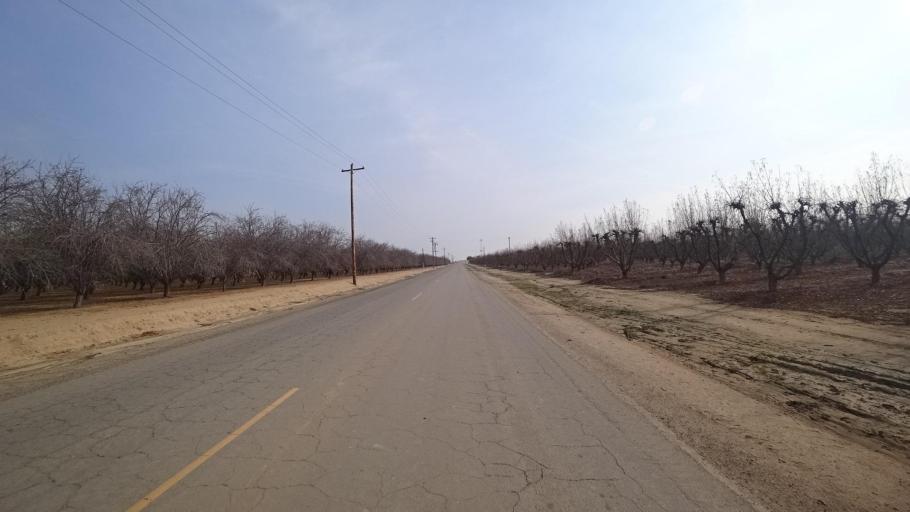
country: US
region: California
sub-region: Kern County
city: Greenfield
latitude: 35.0764
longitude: -119.0264
